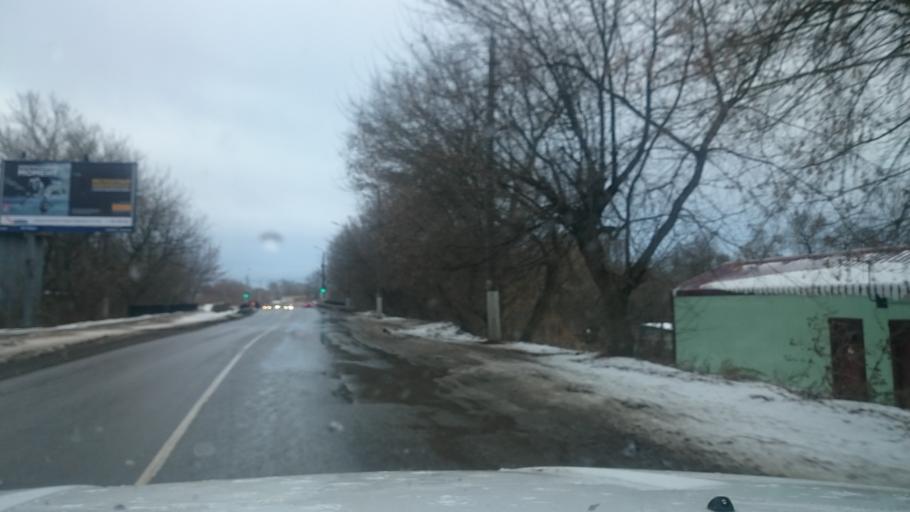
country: RU
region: Tula
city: Tula
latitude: 54.1940
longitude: 37.5670
